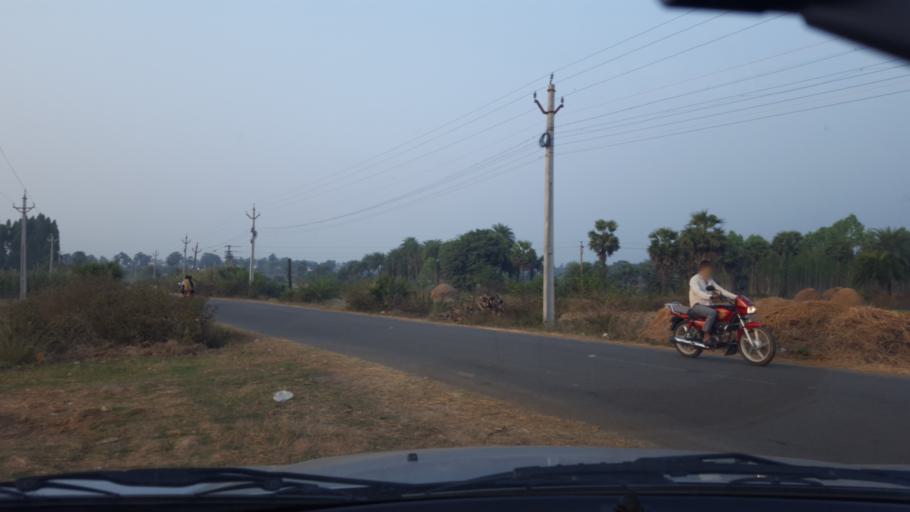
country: IN
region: Andhra Pradesh
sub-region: Srikakulam
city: Amudalavalasa
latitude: 18.3864
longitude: 83.9231
